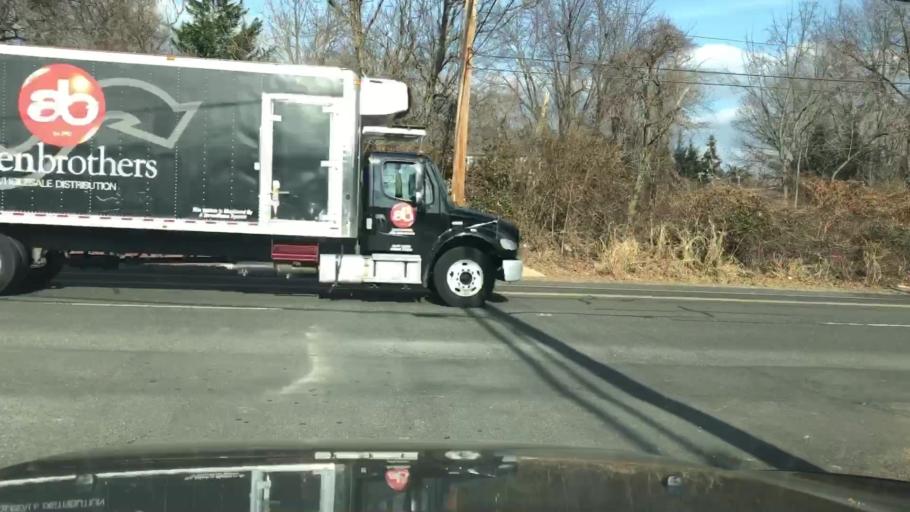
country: US
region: Pennsylvania
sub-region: Bucks County
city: Newtown
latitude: 40.2360
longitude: -74.9388
